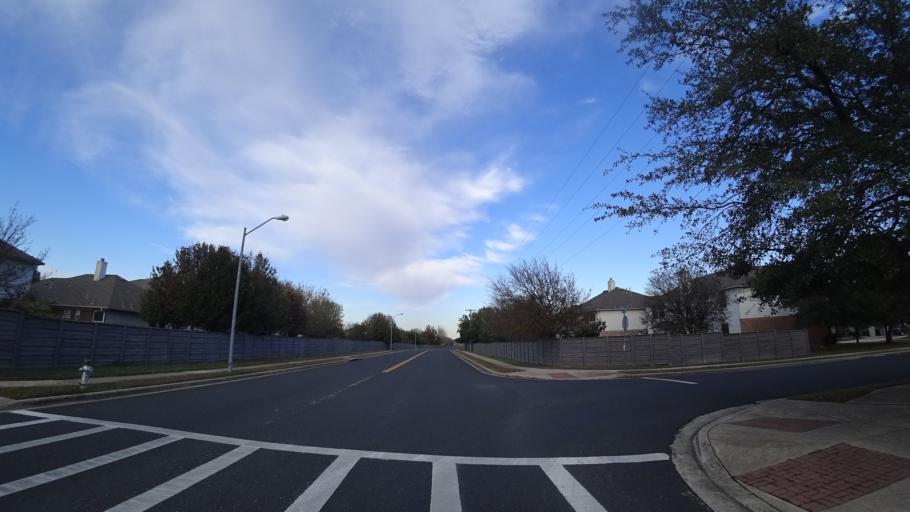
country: US
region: Texas
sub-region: Williamson County
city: Brushy Creek
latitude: 30.4996
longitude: -97.7388
